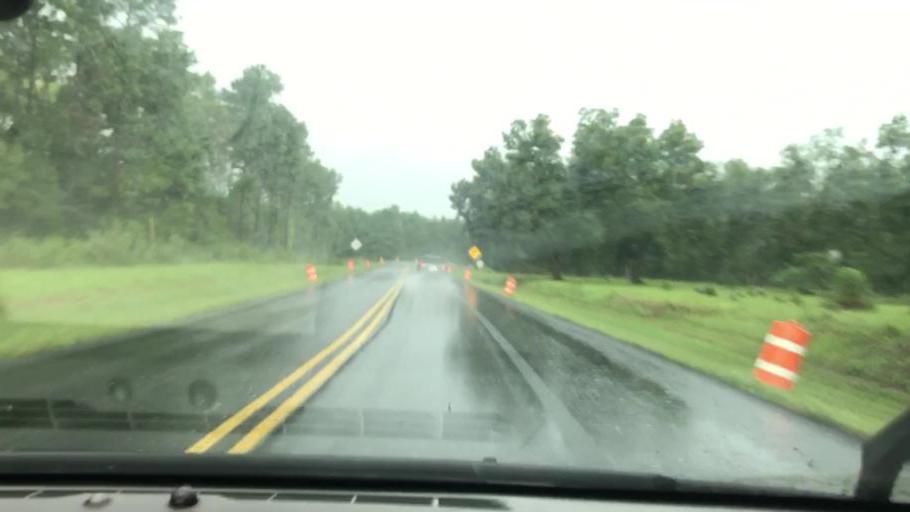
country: US
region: Georgia
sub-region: Clay County
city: Fort Gaines
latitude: 31.5700
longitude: -85.0167
